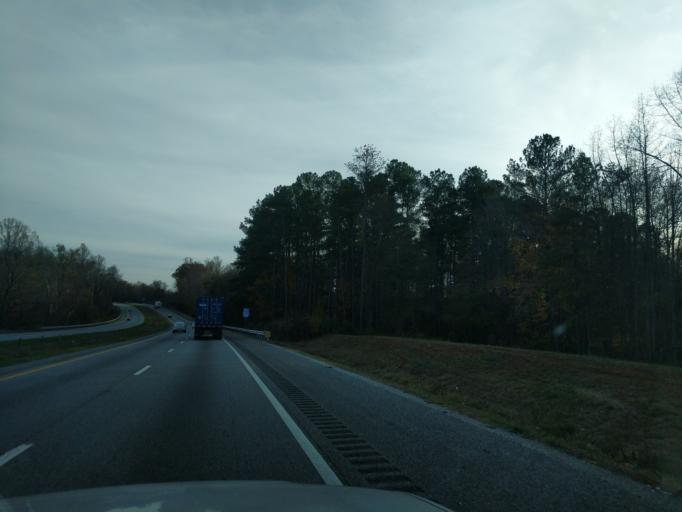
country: US
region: South Carolina
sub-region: Spartanburg County
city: Southern Shops
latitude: 35.0217
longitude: -82.0353
